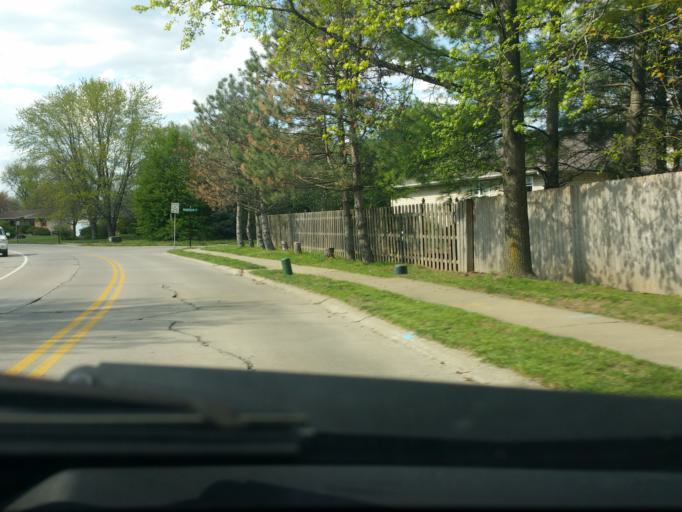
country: US
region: Illinois
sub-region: Madison County
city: Edwardsville
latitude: 38.7897
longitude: -89.9649
